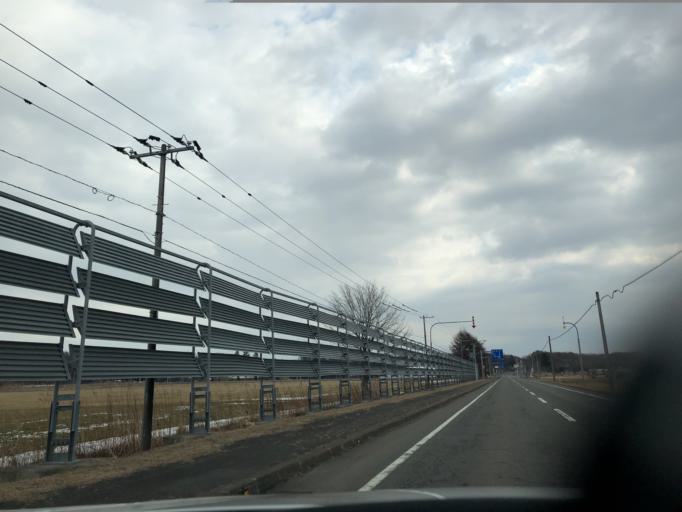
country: JP
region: Hokkaido
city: Chitose
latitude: 42.7620
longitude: 141.7692
